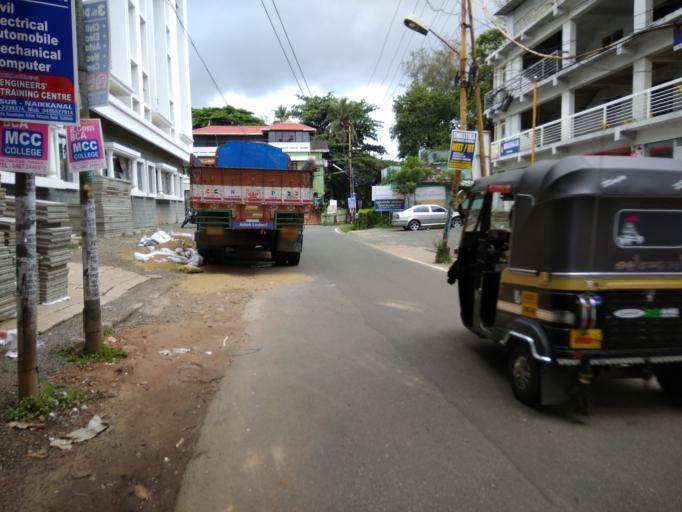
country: IN
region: Kerala
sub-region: Thrissur District
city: Trichur
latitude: 10.5289
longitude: 76.2172
